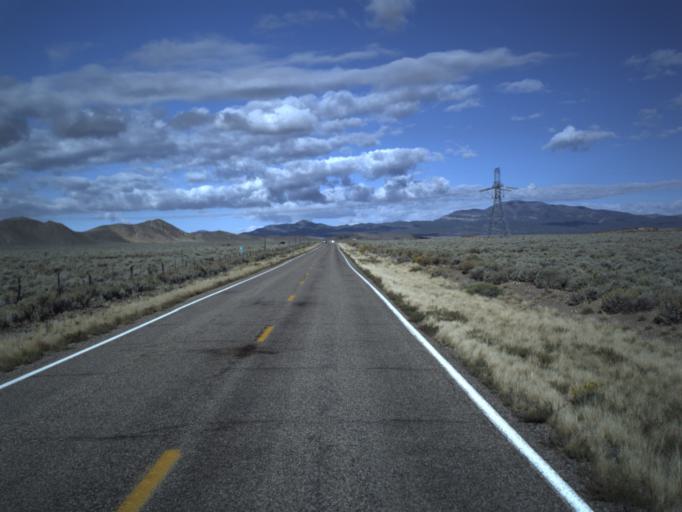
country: US
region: Utah
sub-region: Beaver County
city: Milford
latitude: 38.4094
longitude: -113.0603
